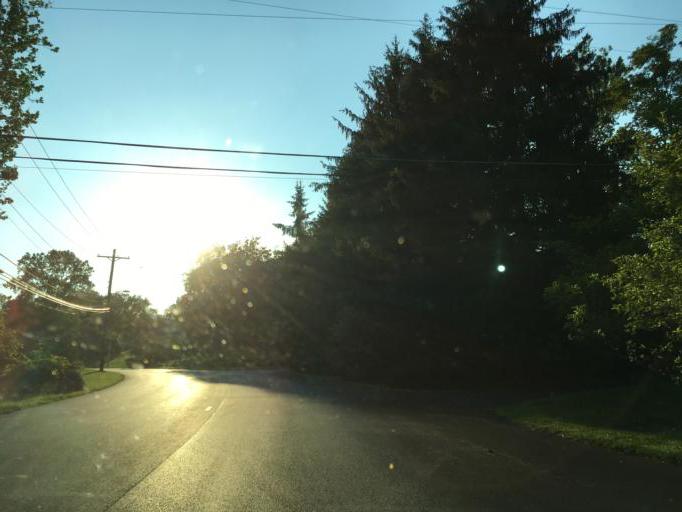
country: US
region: Maryland
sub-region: Baltimore County
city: Hampton
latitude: 39.4251
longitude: -76.5985
